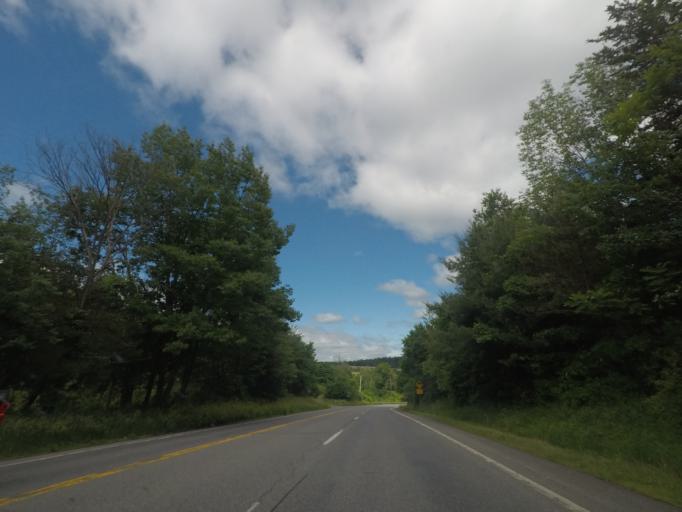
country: US
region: New York
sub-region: Columbia County
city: Philmont
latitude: 42.2097
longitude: -73.6816
